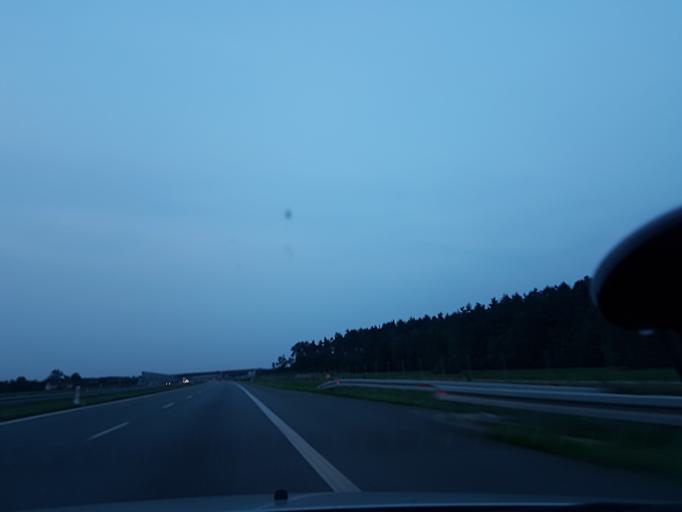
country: PL
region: Lodz Voivodeship
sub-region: Powiat leczycki
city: Piatek
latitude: 52.0227
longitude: 19.5420
